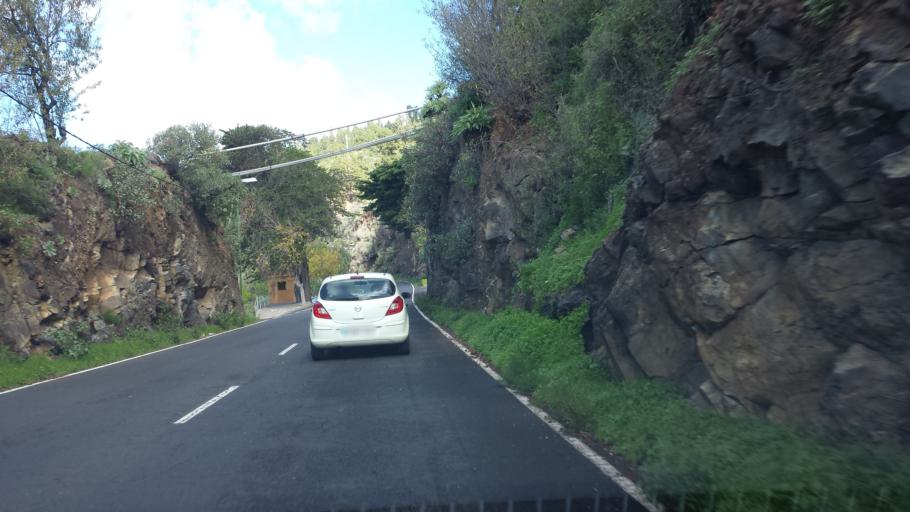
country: ES
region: Canary Islands
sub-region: Provincia de Santa Cruz de Tenerife
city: Tijarafe
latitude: 28.7237
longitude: -17.9591
